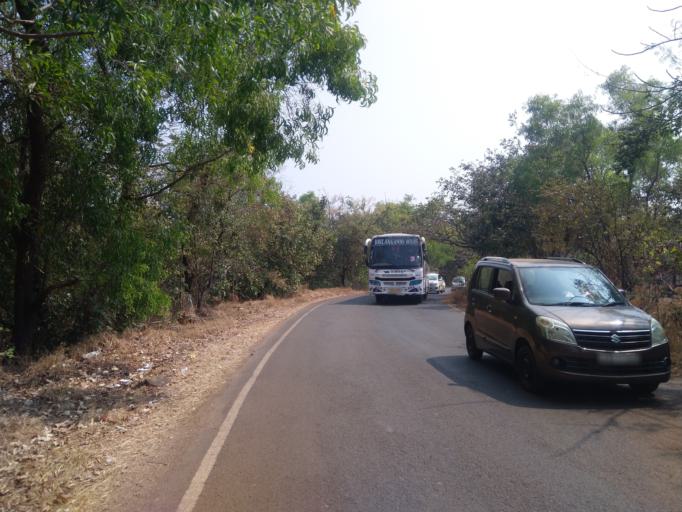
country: IN
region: Goa
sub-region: North Goa
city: Candolim
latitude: 15.4949
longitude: 73.7779
